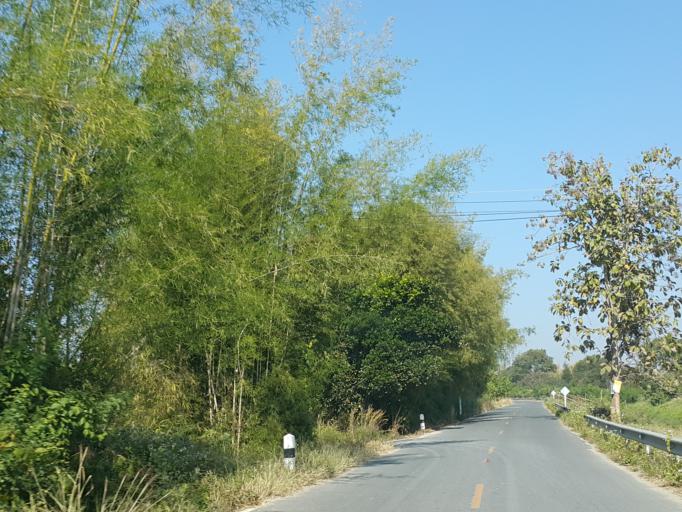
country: TH
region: Chiang Mai
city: San Sai
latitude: 18.9390
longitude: 98.9954
